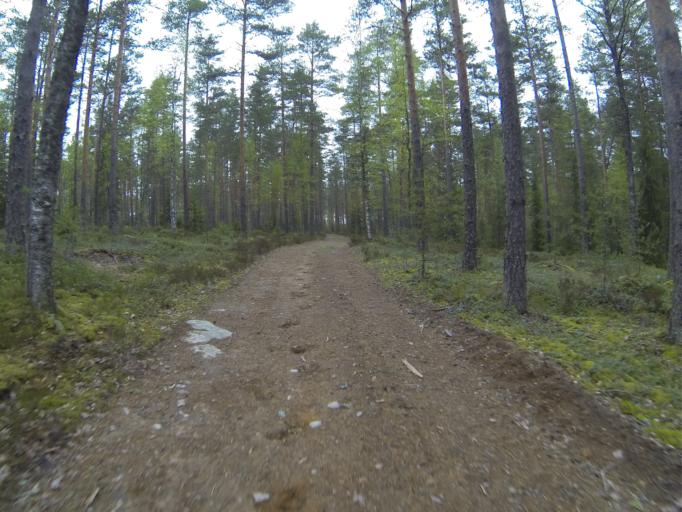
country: FI
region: Varsinais-Suomi
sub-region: Salo
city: Pertteli
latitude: 60.3890
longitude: 23.2133
